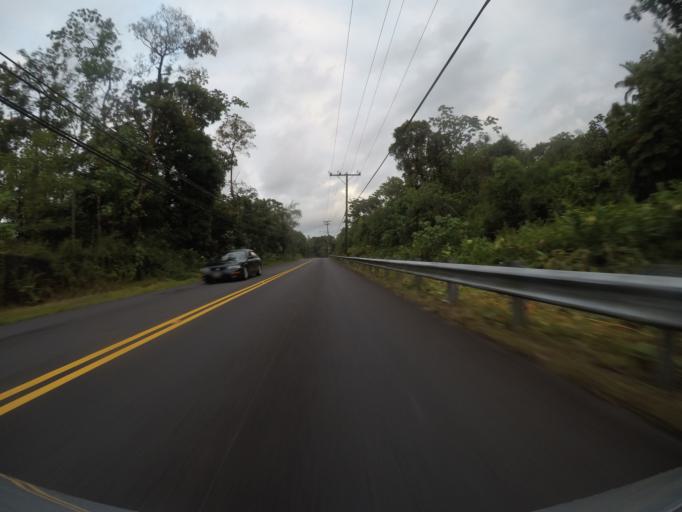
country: US
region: Hawaii
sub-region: Hawaii County
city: Kea'au
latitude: 19.6721
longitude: -155.0657
